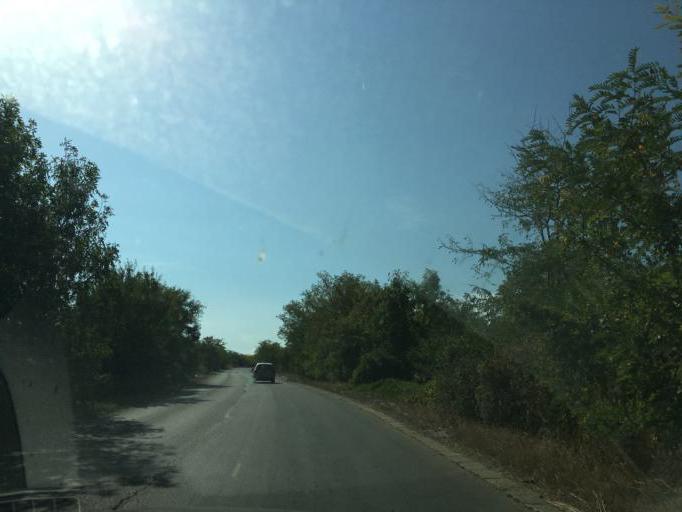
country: BG
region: Pazardzhik
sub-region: Obshtina Peshtera
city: Peshtera
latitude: 42.1078
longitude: 24.2973
